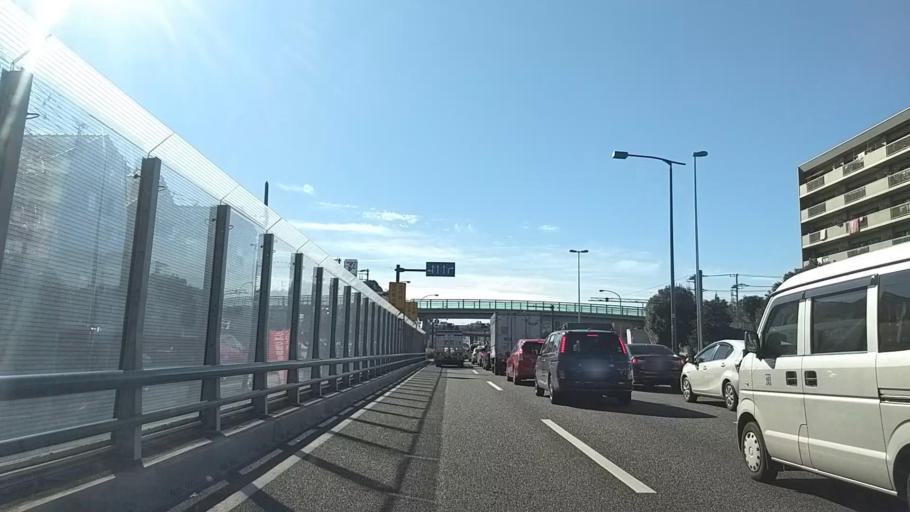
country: JP
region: Kanagawa
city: Yokohama
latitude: 35.4644
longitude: 139.5644
